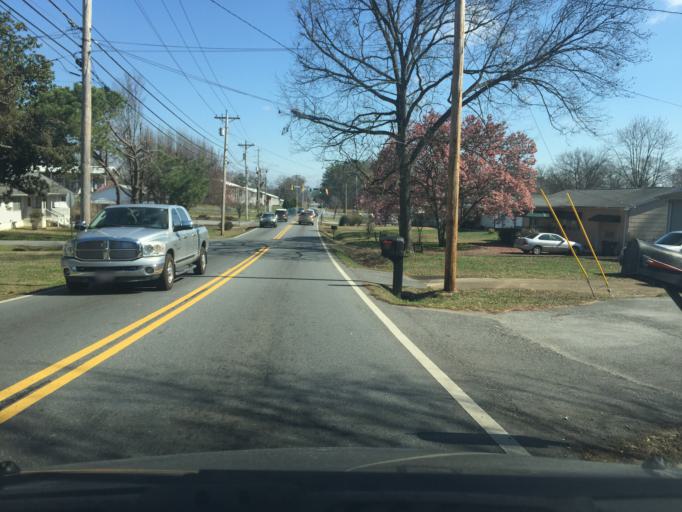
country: US
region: Georgia
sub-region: Catoosa County
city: Fort Oglethorpe
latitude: 34.9634
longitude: -85.2576
